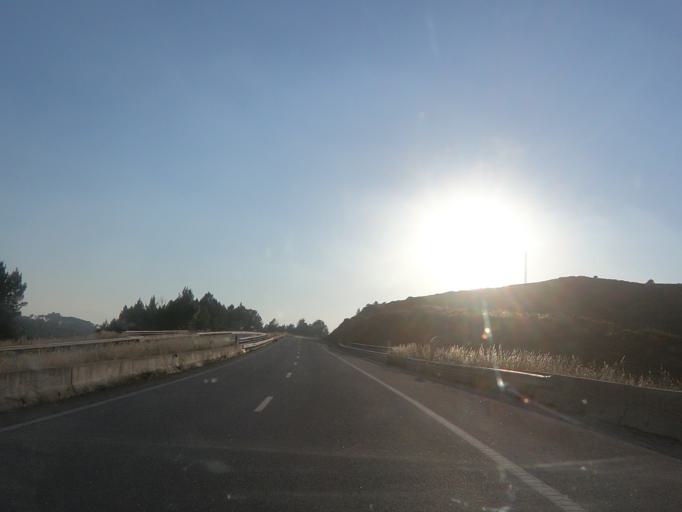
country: PT
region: Guarda
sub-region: Celorico da Beira
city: Celorico da Beira
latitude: 40.6325
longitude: -7.4345
